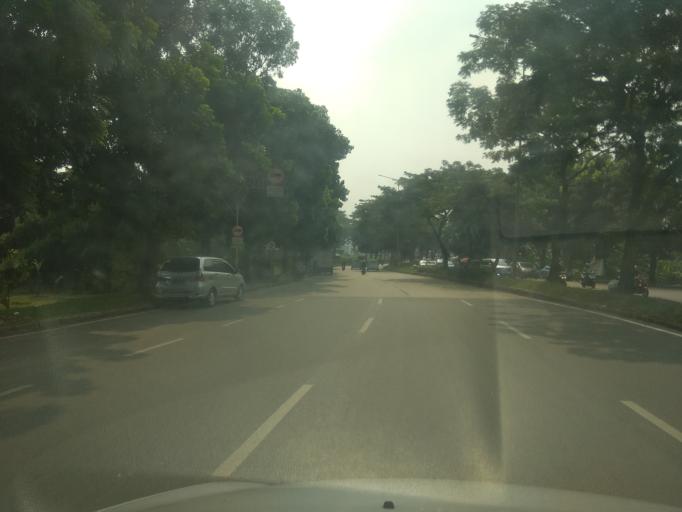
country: ID
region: West Java
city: Serpong
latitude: -6.3080
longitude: 106.6876
